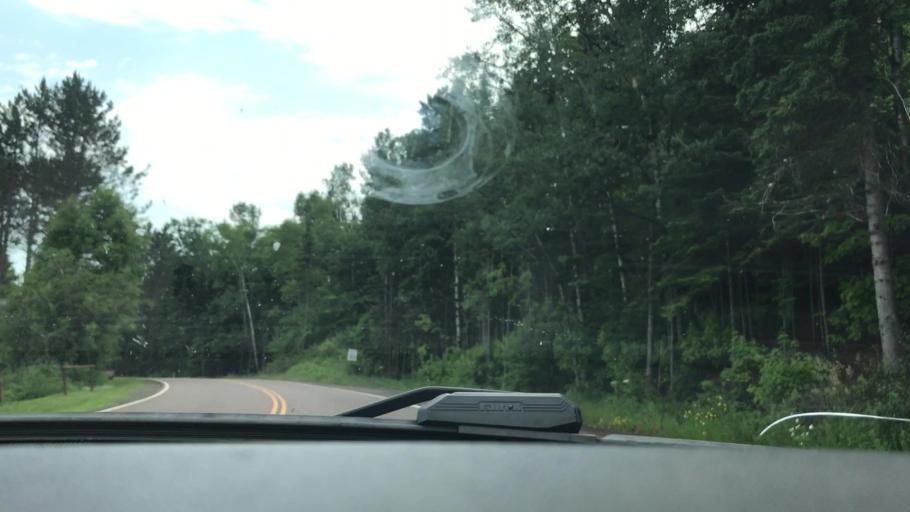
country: CA
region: Ontario
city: Neebing
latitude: 47.9627
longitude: -89.6857
